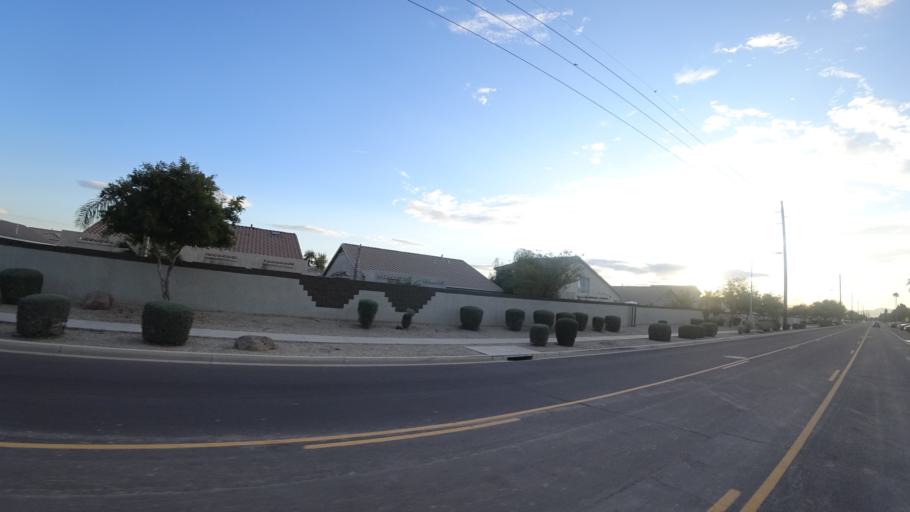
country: US
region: Arizona
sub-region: Maricopa County
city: Glendale
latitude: 33.5451
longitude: -112.2223
